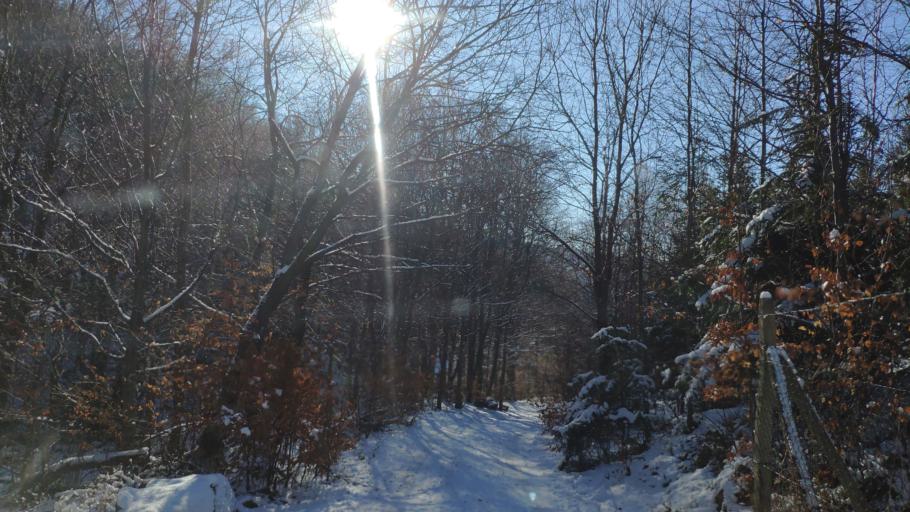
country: SK
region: Kosicky
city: Gelnica
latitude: 48.7584
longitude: 21.0073
